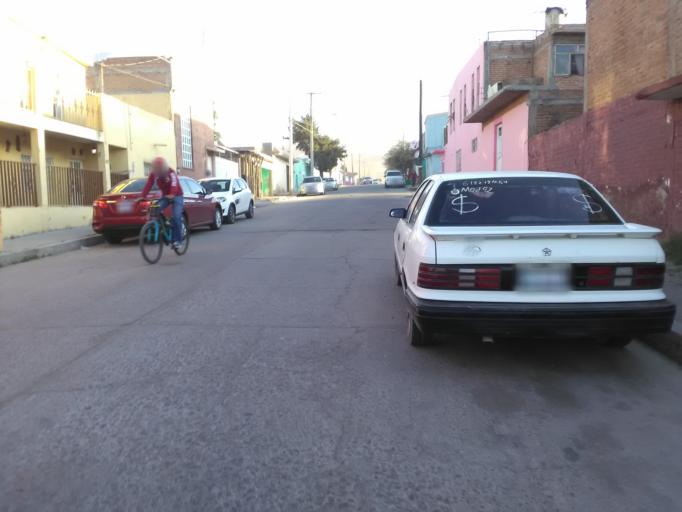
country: MX
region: Durango
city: Victoria de Durango
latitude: 24.0425
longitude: -104.6685
